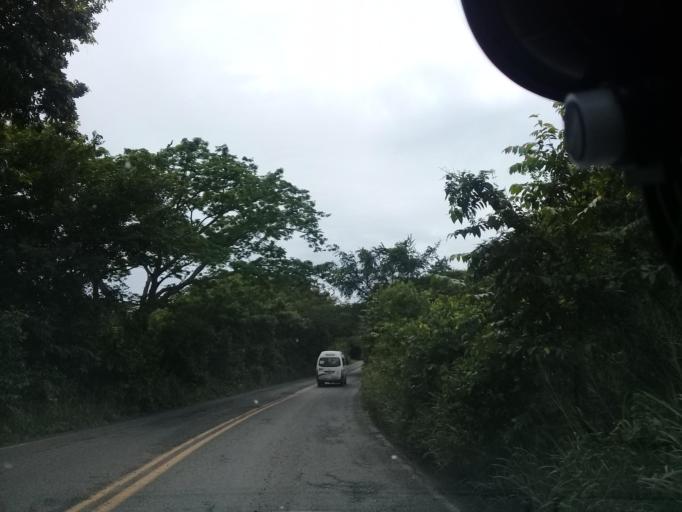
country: MX
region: Veracruz
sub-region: Chalma
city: San Pedro Coyutla
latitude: 21.2054
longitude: -98.3875
